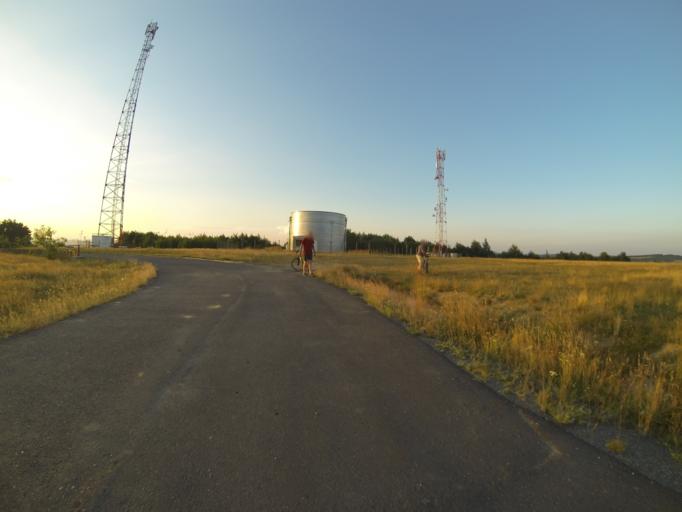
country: RO
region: Brasov
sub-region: Comuna Sinca Veche
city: Sinca Veche
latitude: 45.7548
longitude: 25.1694
